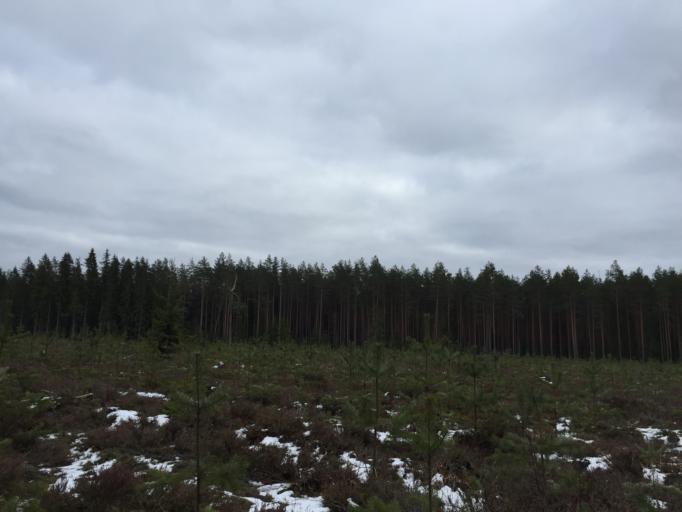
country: LV
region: Garkalne
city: Garkalne
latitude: 56.9649
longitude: 24.4751
